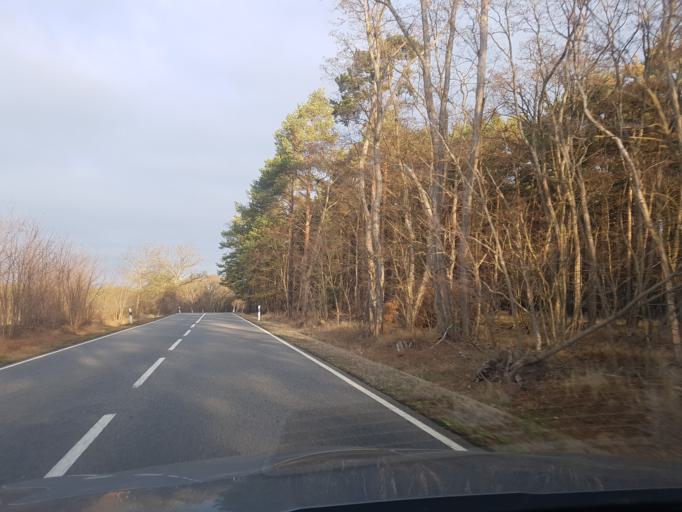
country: DE
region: Brandenburg
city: Kasel-Golzig
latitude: 51.9120
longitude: 13.6703
